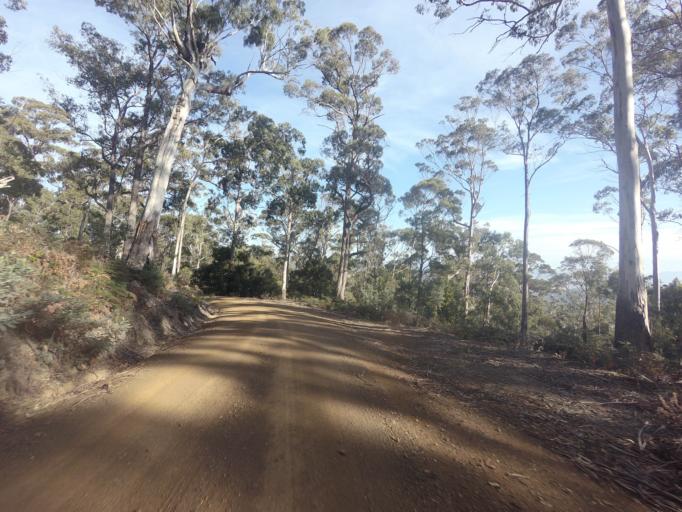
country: AU
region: Tasmania
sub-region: Sorell
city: Sorell
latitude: -42.5249
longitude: 147.4630
